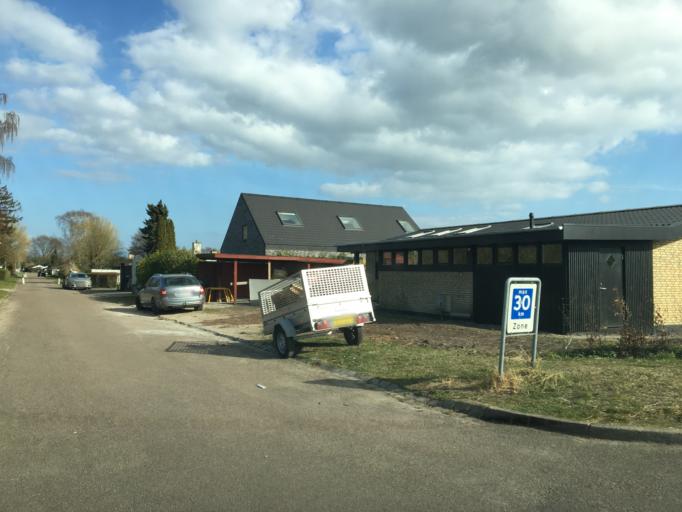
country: DK
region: Capital Region
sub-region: Dragor Kommune
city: Dragor
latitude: 55.5993
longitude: 12.6626
